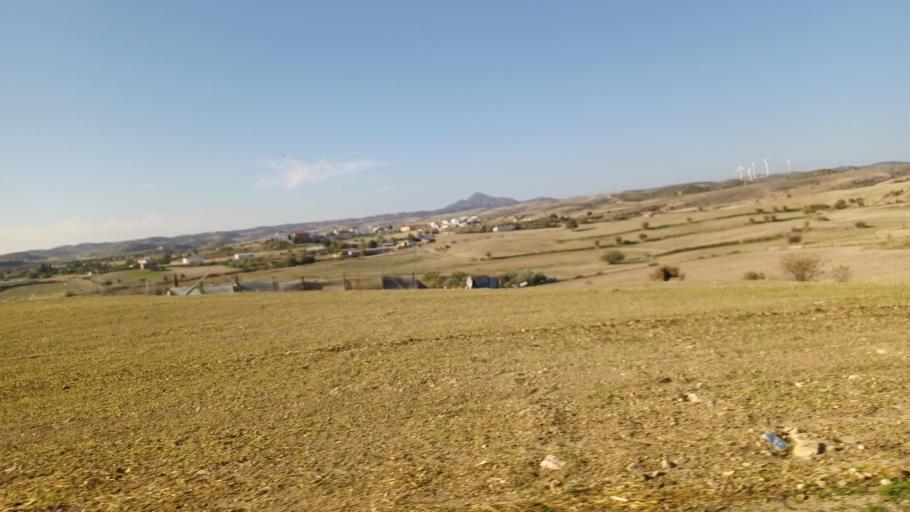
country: CY
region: Larnaka
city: Aradippou
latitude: 34.9345
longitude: 33.5306
